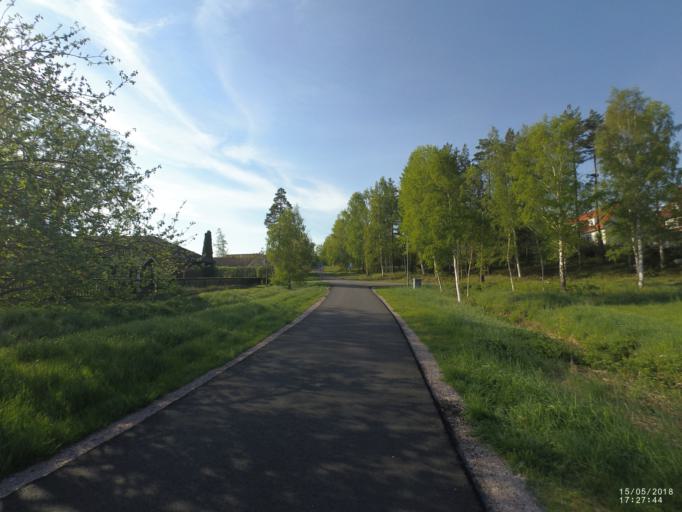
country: SE
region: Soedermanland
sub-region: Nykopings Kommun
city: Nykoping
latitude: 58.7257
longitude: 17.0254
